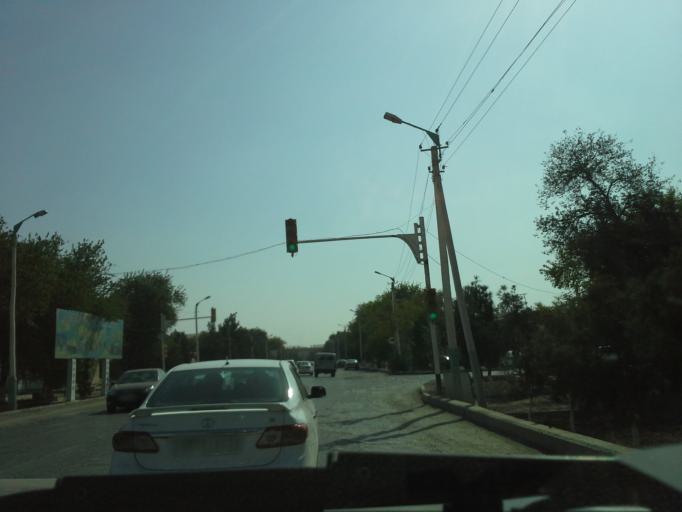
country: TM
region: Lebap
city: Atamyrat
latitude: 37.8389
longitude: 65.2101
